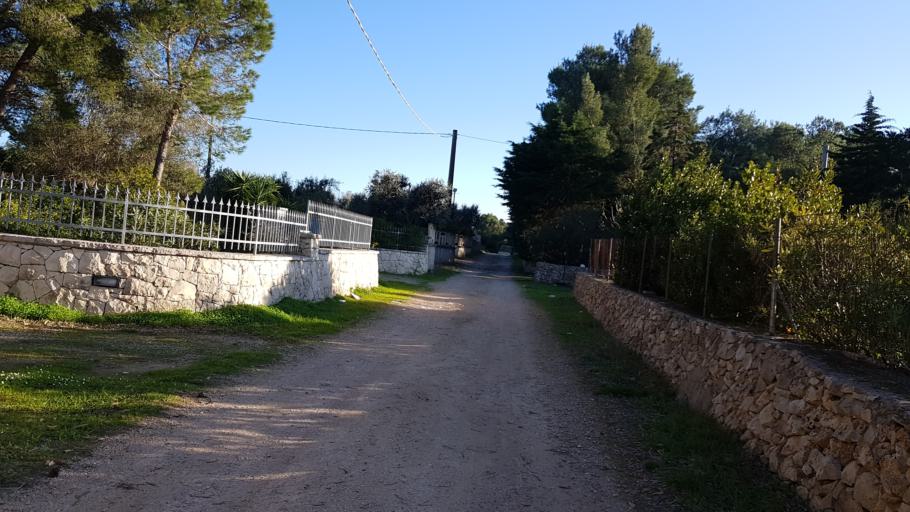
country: IT
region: Apulia
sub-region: Provincia di Lecce
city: Nardo
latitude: 40.1559
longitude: 17.9752
